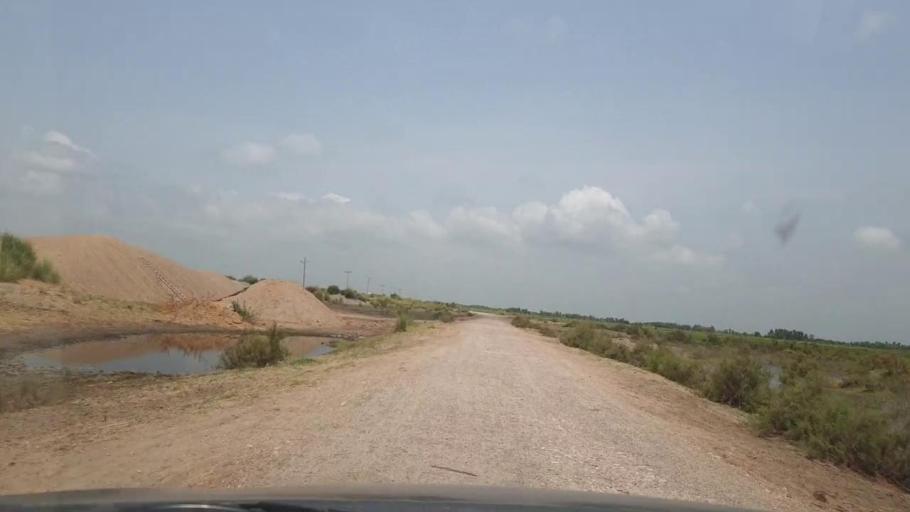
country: PK
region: Sindh
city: Ratodero
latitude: 27.9116
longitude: 68.3011
